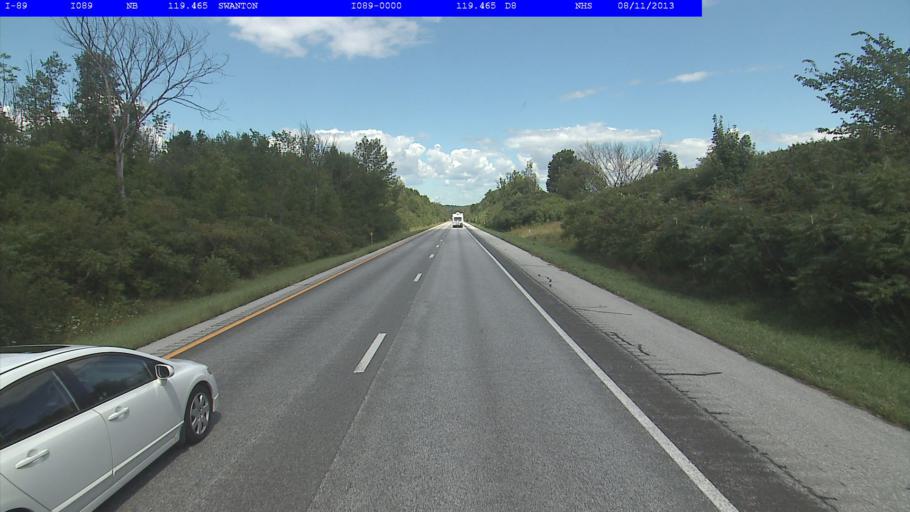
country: US
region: Vermont
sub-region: Franklin County
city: Saint Albans
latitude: 44.8695
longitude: -73.0817
